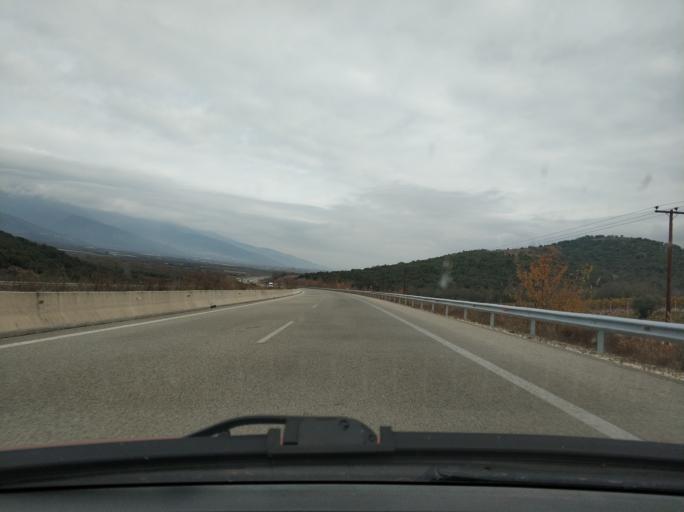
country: GR
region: Central Macedonia
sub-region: Nomos Serron
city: Rodolivos
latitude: 40.8122
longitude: 24.0442
